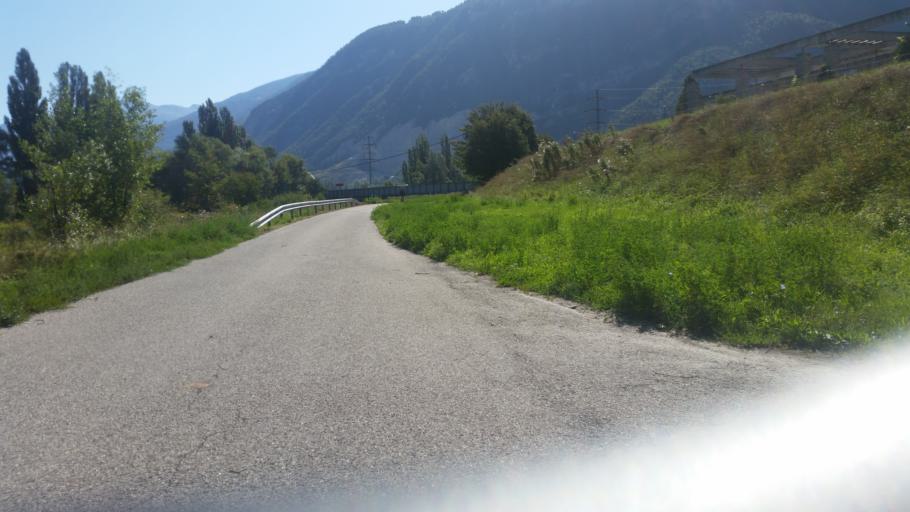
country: CH
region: Valais
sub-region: Sion District
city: Saint-Leonard
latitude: 46.2439
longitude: 7.4044
